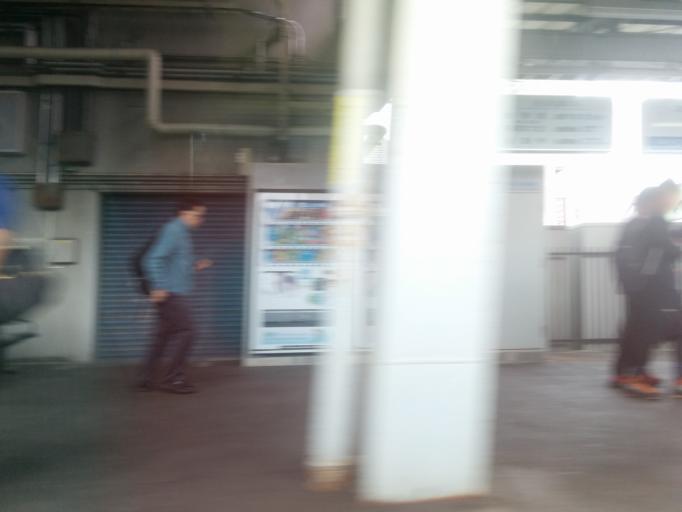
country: JP
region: Shiga Prefecture
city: Hikone
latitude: 35.2724
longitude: 136.2633
